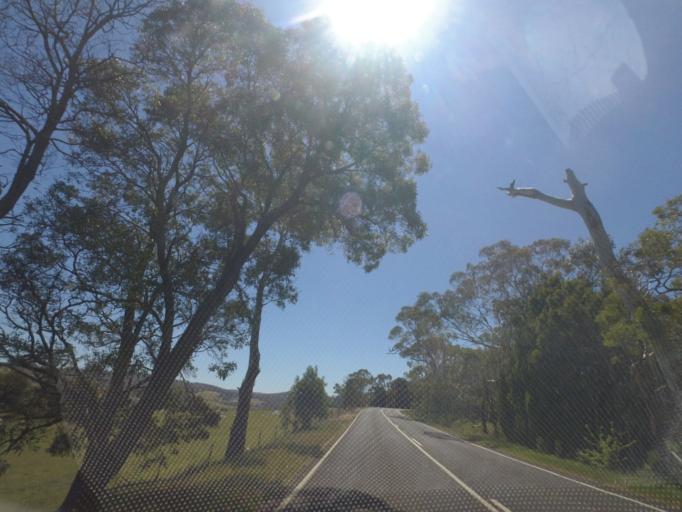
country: AU
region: Victoria
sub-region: Hume
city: Sunbury
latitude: -37.1990
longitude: 144.7394
